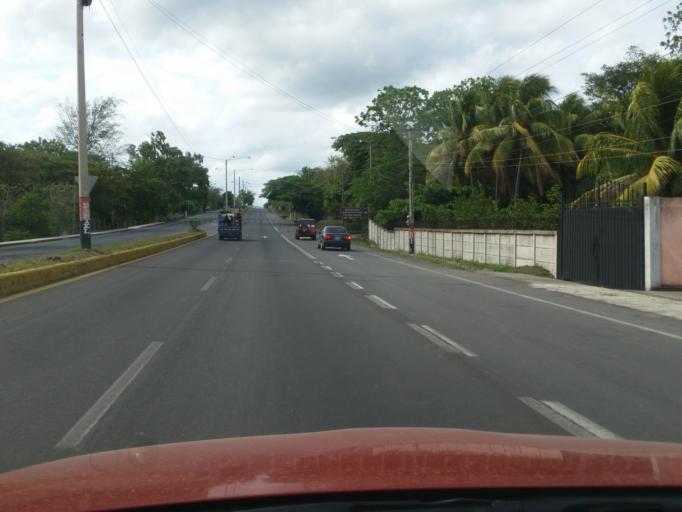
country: NI
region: Masaya
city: Nindiri
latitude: 12.0140
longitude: -86.1425
